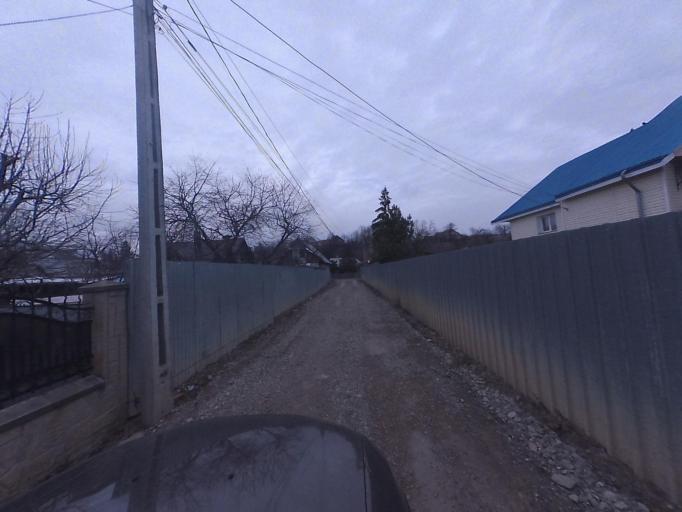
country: RO
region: Neamt
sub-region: Oras Targu Neamt
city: Targu Neamt
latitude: 47.2090
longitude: 26.3768
